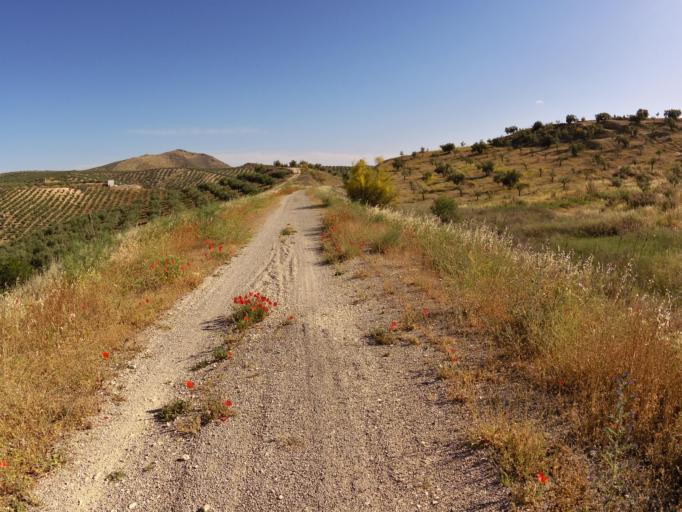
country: ES
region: Andalusia
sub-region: Province of Cordoba
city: Fuente-Tojar
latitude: 37.5829
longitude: -4.1766
